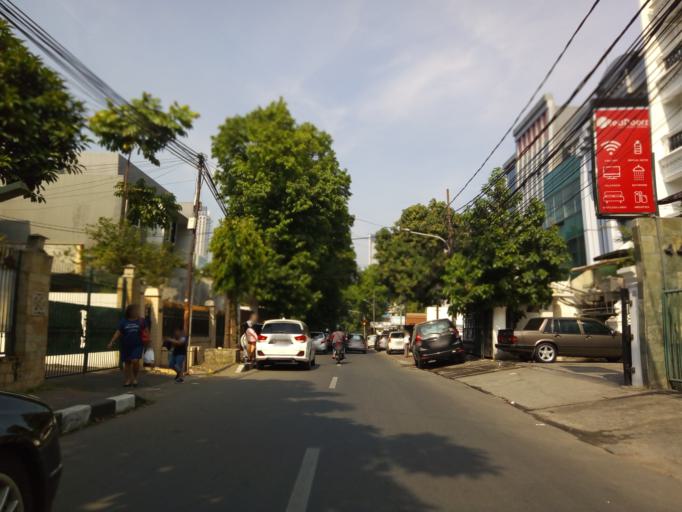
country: ID
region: Jakarta Raya
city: Jakarta
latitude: -6.2086
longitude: 106.8369
